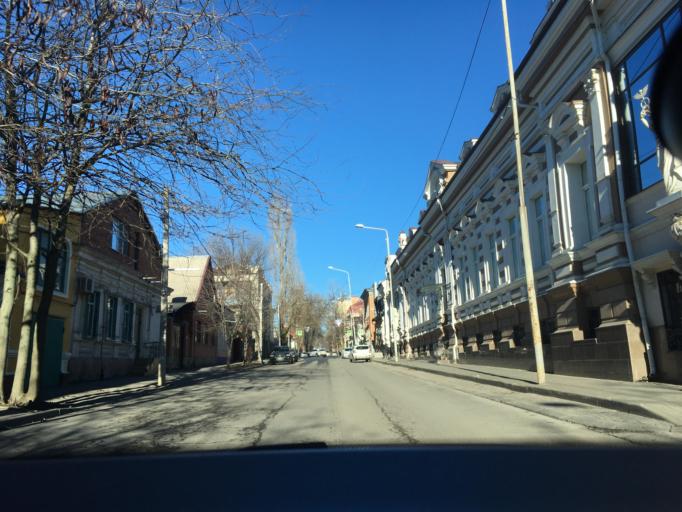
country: RU
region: Rostov
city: Rostov-na-Donu
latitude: 47.2304
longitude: 39.7572
